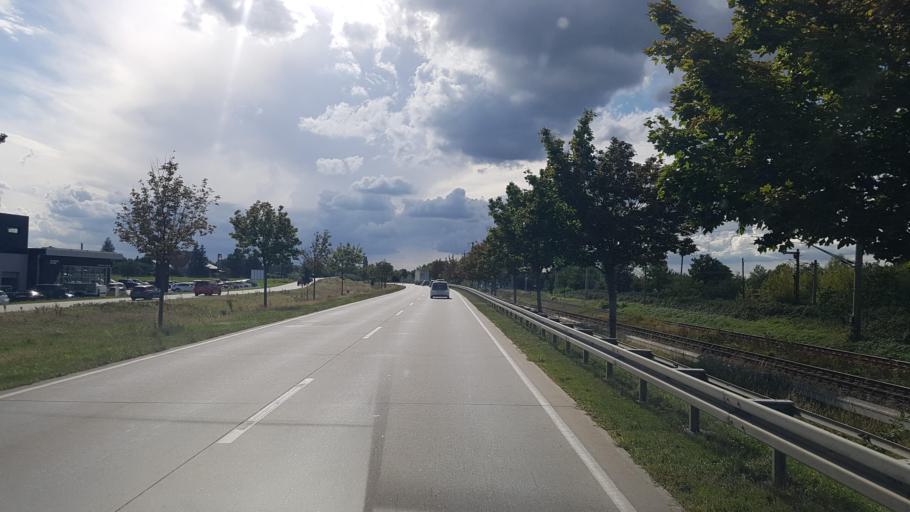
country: DE
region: Saxony
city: Thallwitz
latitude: 51.4653
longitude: 12.6730
